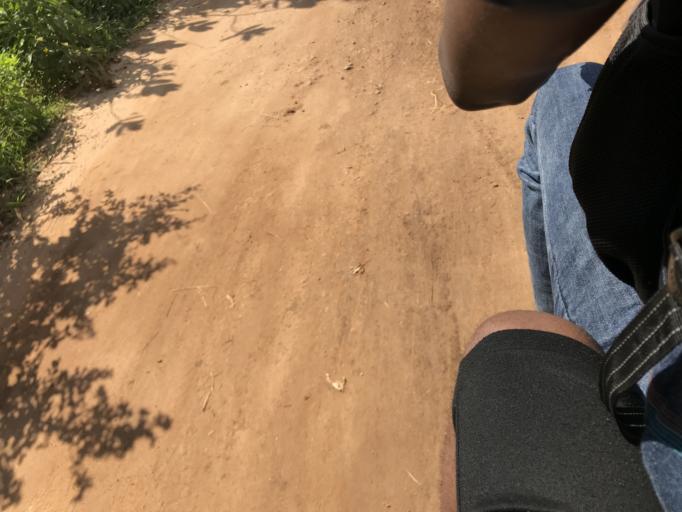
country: TZ
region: Dar es Salaam
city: Dar es Salaam
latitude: -6.8799
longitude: 39.4399
